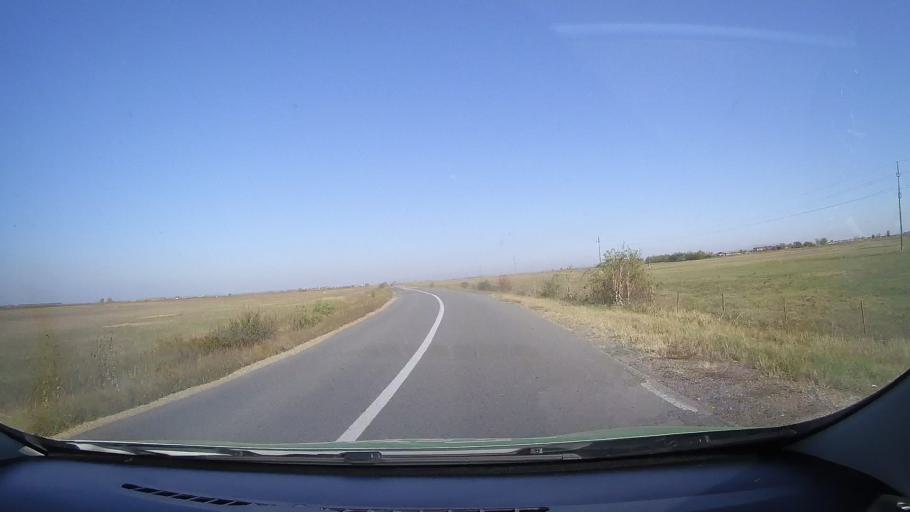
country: RO
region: Satu Mare
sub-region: Comuna Cauas
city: Cauas
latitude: 47.5415
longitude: 22.5641
